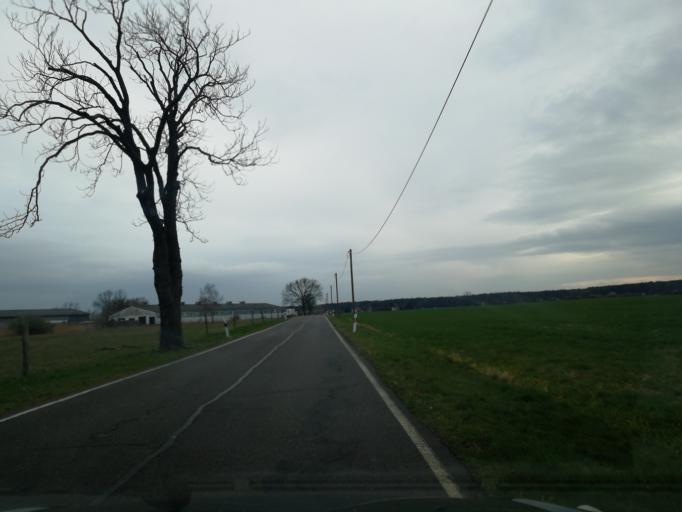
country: DE
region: Brandenburg
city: Calau
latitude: 51.7373
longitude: 14.0215
